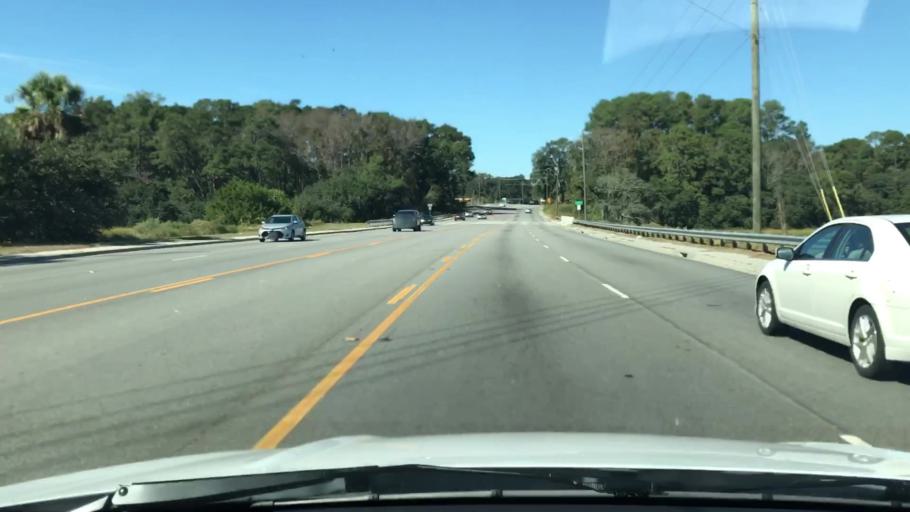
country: US
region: South Carolina
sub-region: Beaufort County
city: Burton
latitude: 32.4492
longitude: -80.7310
